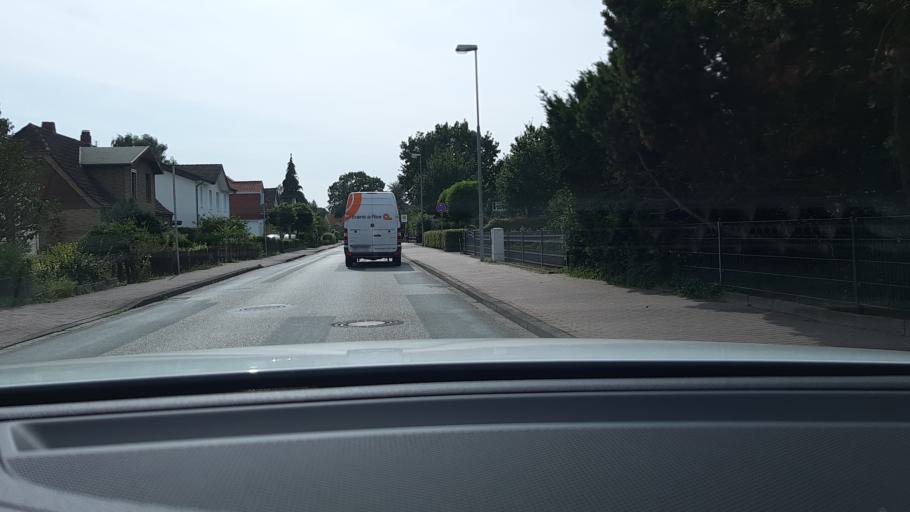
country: DE
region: Schleswig-Holstein
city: Stockelsdorf
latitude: 53.8969
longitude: 10.6536
